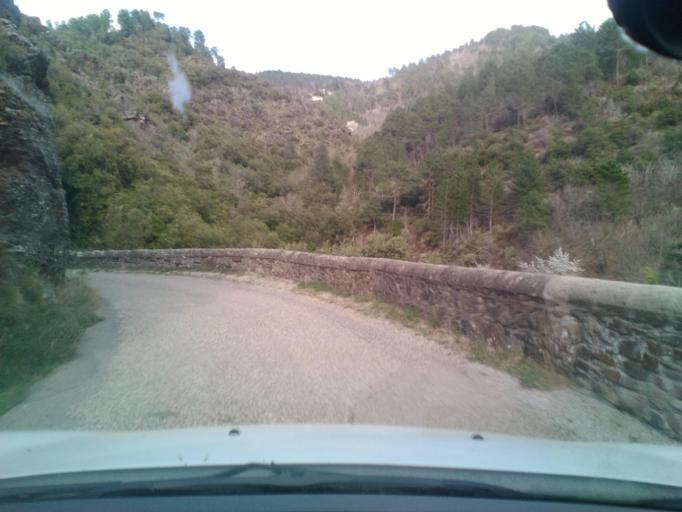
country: FR
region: Languedoc-Roussillon
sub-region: Departement du Gard
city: Saint-Jean-du-Gard
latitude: 44.1372
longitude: 3.7660
